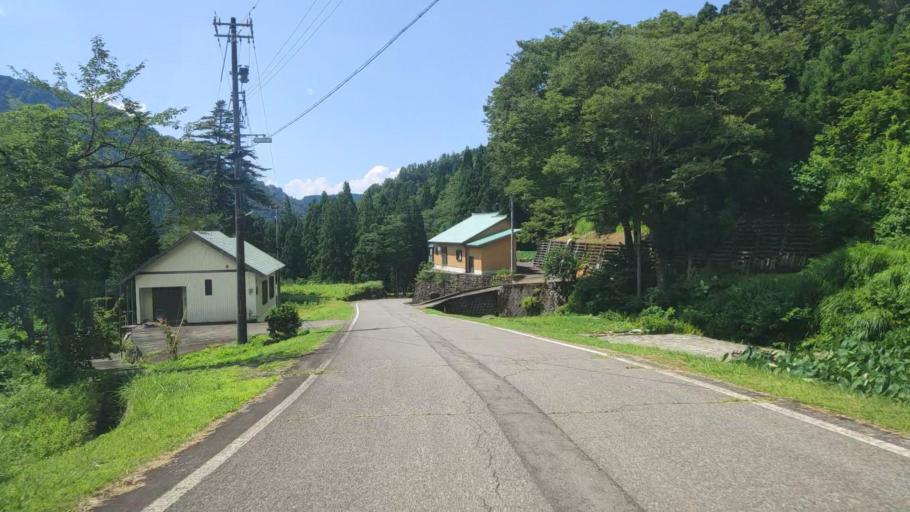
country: JP
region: Fukui
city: Katsuyama
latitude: 36.1247
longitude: 136.5078
